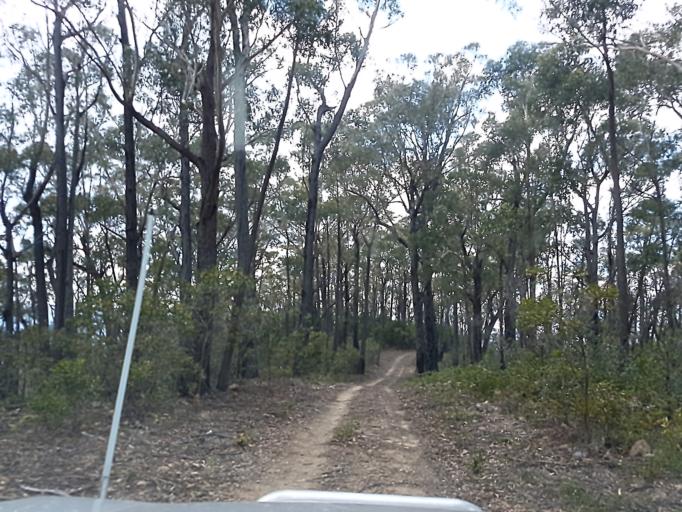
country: AU
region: Victoria
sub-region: East Gippsland
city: Lakes Entrance
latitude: -37.3457
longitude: 148.3393
